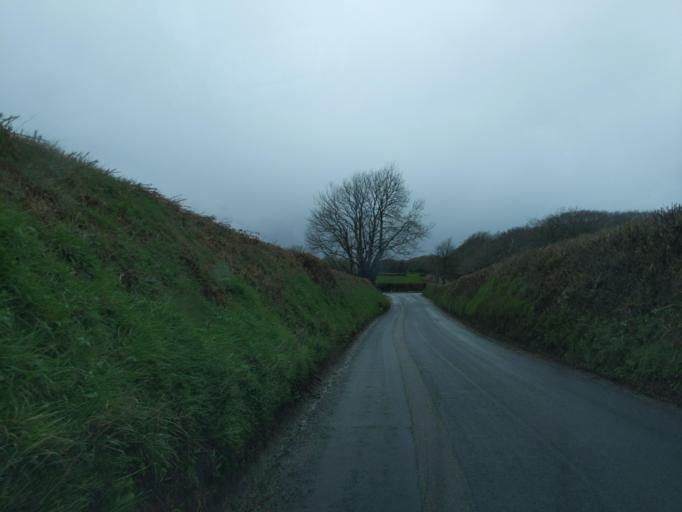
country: GB
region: England
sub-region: Cornwall
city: North Hill
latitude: 50.5868
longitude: -4.4358
